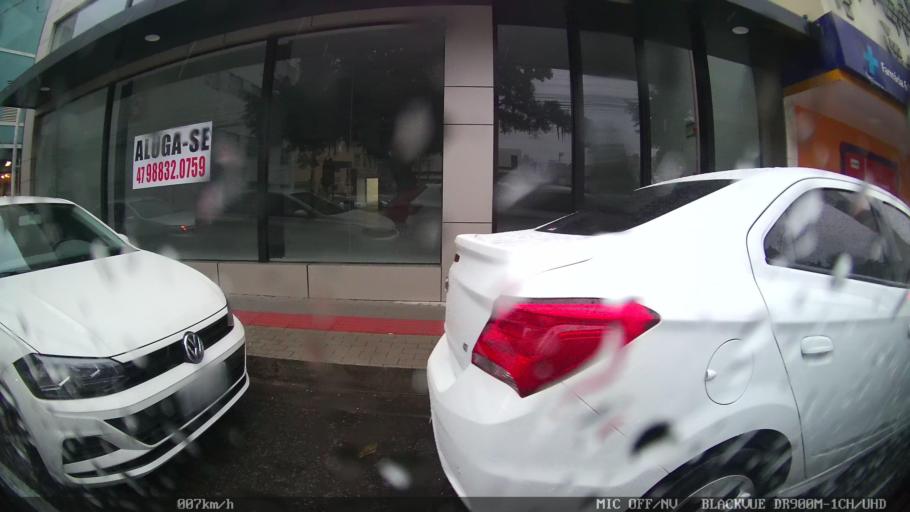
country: BR
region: Santa Catarina
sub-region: Itajai
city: Itajai
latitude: -26.9064
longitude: -48.6575
